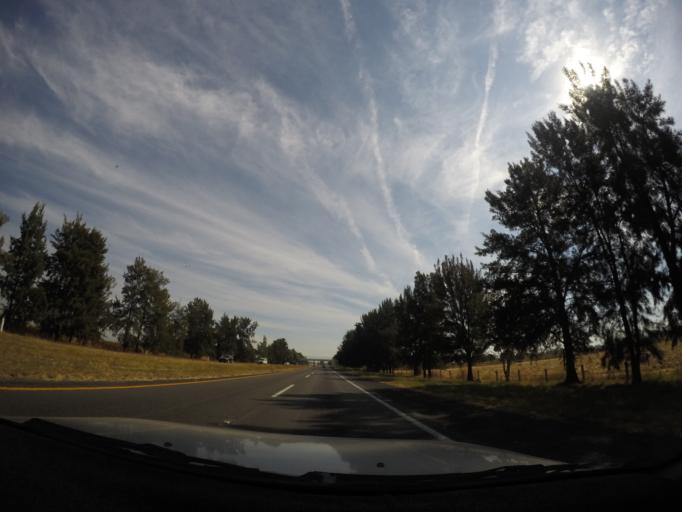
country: MX
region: Michoacan
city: Vistahermosa de Negrete
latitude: 20.2896
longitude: -102.4698
